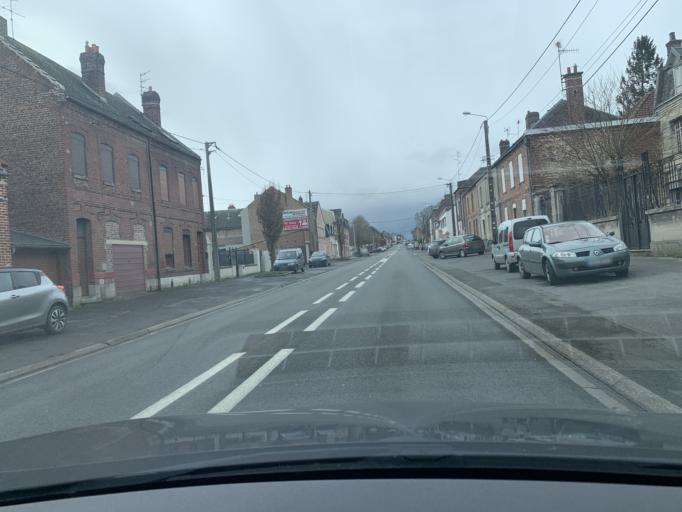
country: FR
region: Nord-Pas-de-Calais
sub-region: Departement du Nord
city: Neuville-Saint-Remy
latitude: 50.1797
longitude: 3.2086
